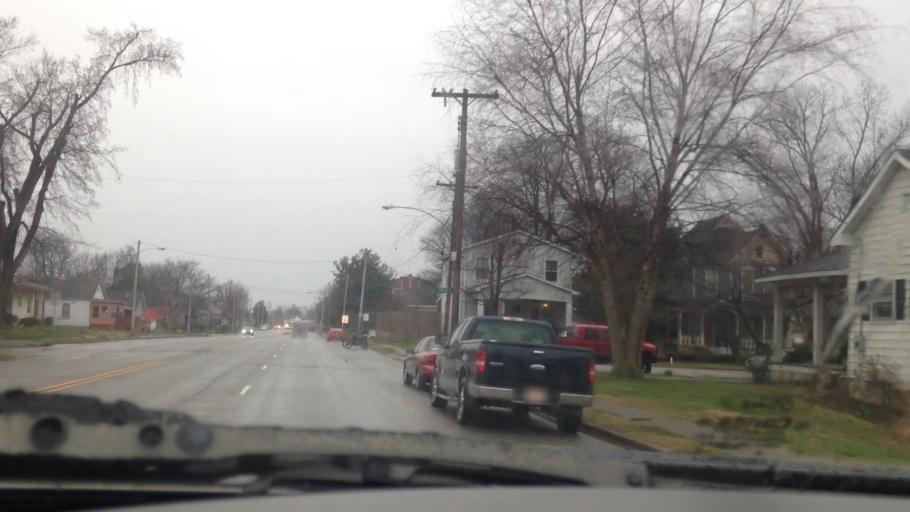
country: US
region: Illinois
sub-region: Massac County
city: Metropolis
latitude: 37.1499
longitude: -88.7298
